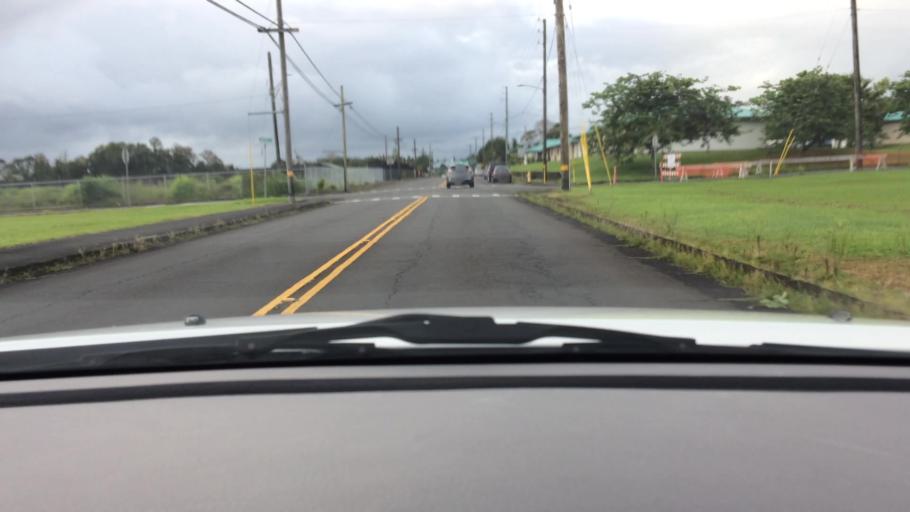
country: US
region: Hawaii
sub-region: Hawaii County
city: Hilo
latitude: 19.7128
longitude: -155.0848
